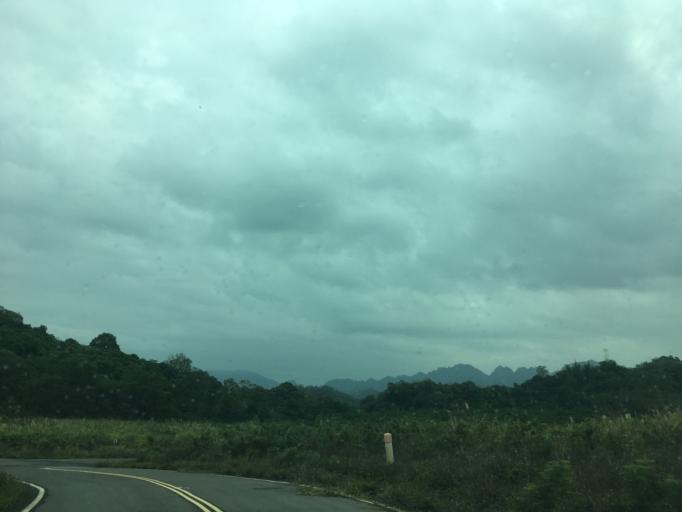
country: TW
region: Taiwan
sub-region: Taichung City
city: Taichung
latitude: 24.0582
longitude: 120.7273
